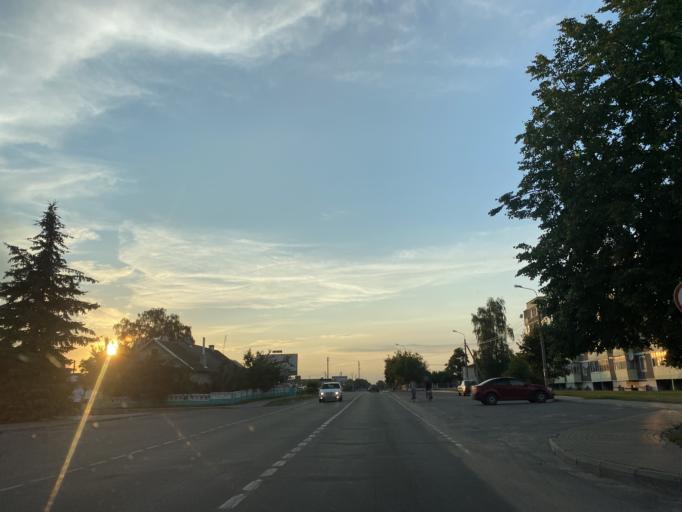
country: BY
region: Brest
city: Ivatsevichy
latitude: 52.7079
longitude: 25.3554
